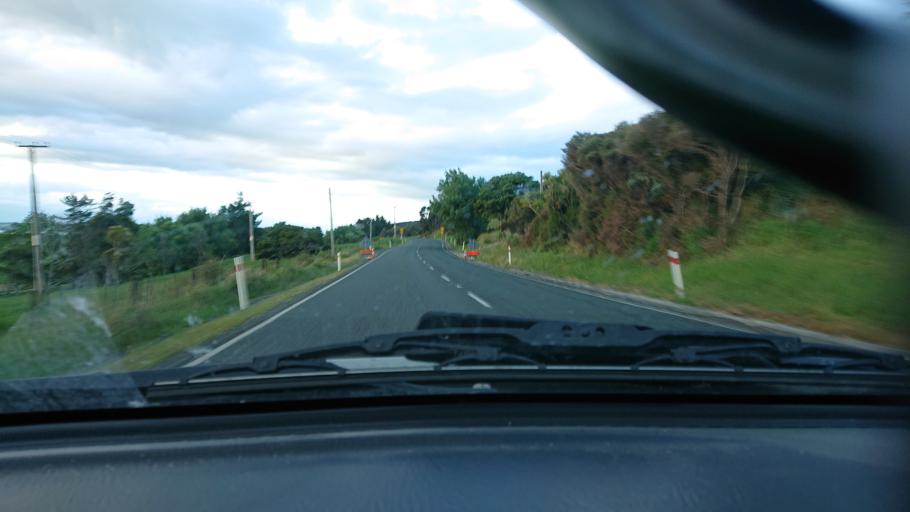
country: NZ
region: Auckland
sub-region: Auckland
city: Wellsford
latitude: -36.4448
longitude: 174.4325
